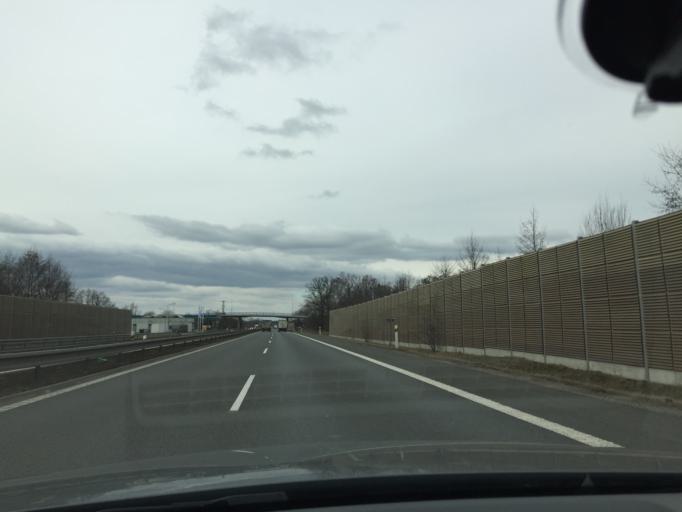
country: CZ
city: Dobra
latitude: 49.6822
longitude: 18.3883
